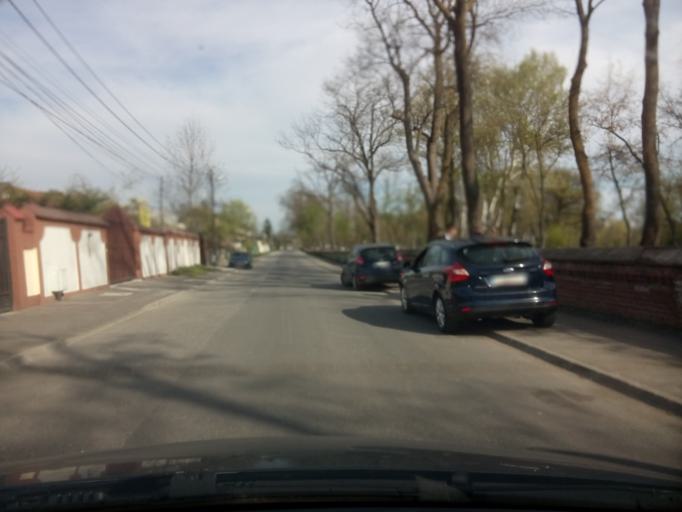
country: RO
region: Ilfov
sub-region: Comuna Mogosoaia
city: Mogosoaia
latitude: 44.5261
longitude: 25.9991
